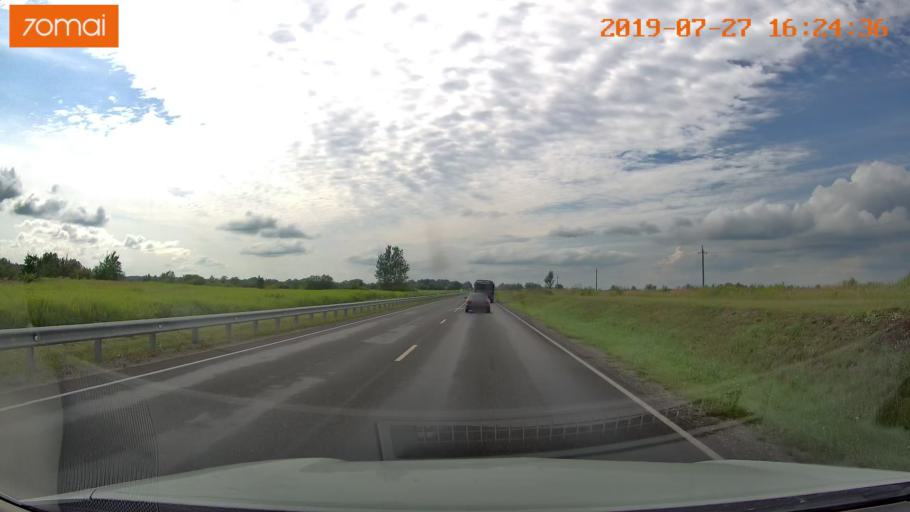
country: RU
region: Kaliningrad
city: Zheleznodorozhnyy
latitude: 54.6346
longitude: 21.4492
